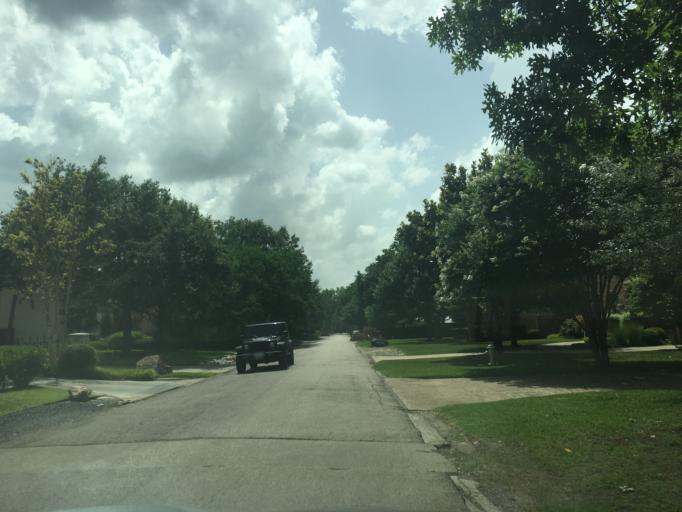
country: US
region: Texas
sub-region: Dallas County
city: University Park
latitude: 32.8885
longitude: -96.7996
